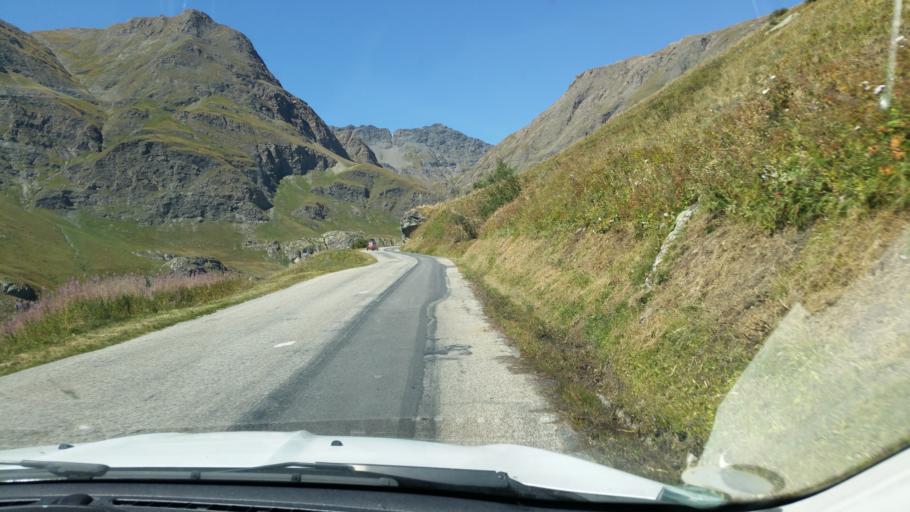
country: FR
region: Rhone-Alpes
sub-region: Departement de la Savoie
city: Val-d'Isere
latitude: 45.3881
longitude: 7.0436
